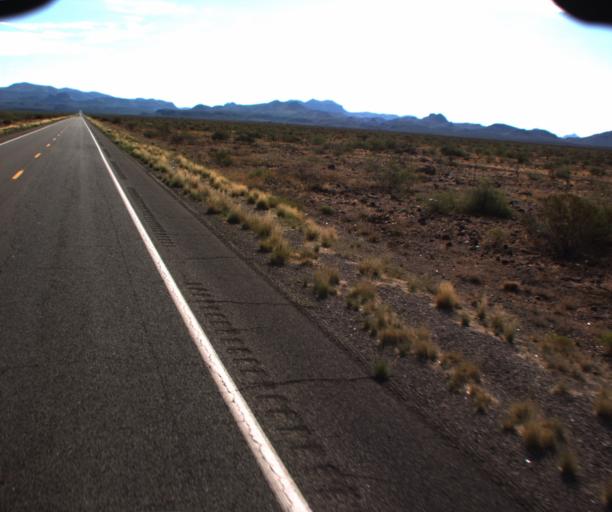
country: US
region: Arizona
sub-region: Graham County
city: Safford
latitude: 32.8175
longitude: -109.4842
